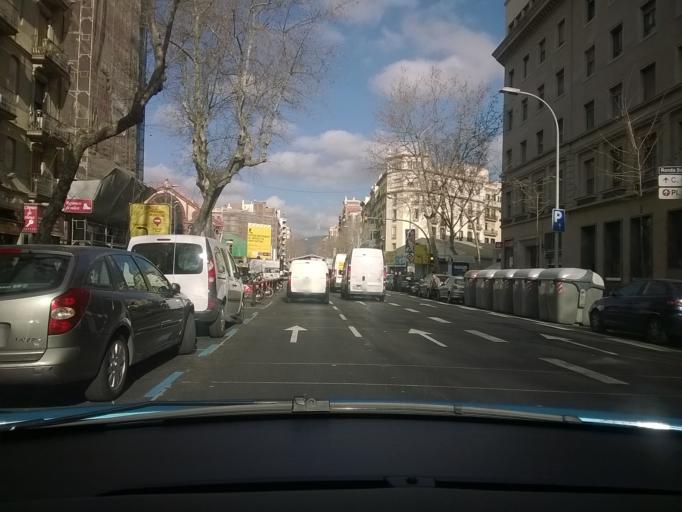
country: ES
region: Catalonia
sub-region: Provincia de Barcelona
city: Ciutat Vella
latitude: 41.3783
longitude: 2.1637
